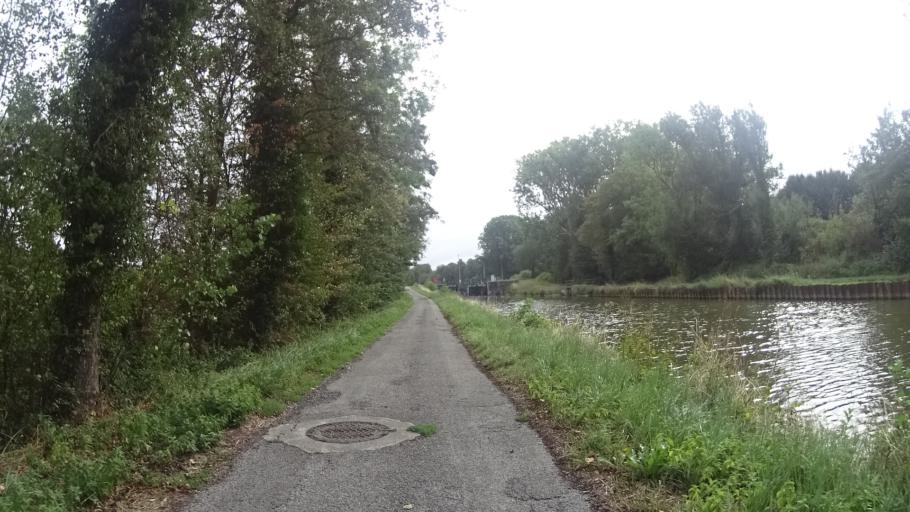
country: FR
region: Picardie
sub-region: Departement de l'Aisne
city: Etreux
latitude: 49.9941
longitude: 3.6590
